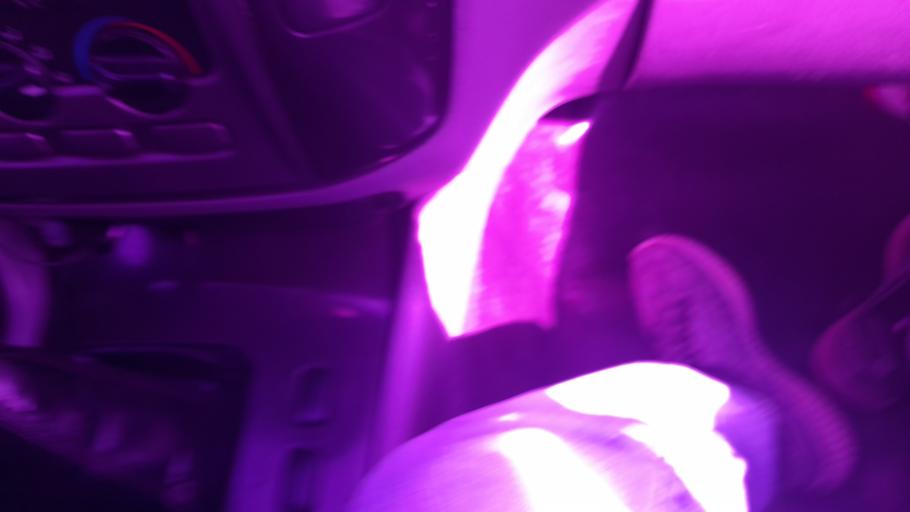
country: ET
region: Southern Nations, Nationalities, and People's Region
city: Bonga
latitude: 7.4836
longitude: 36.4598
